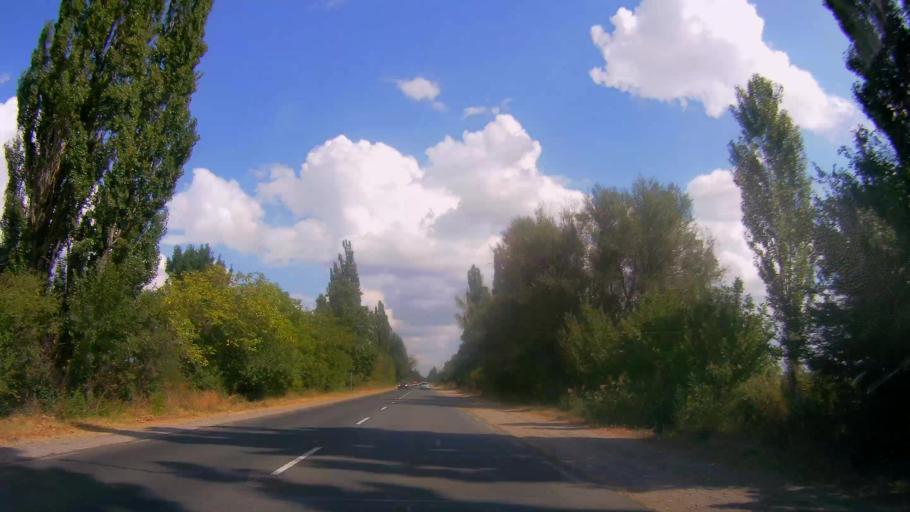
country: BG
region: Sliven
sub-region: Obshtina Sliven
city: Sliven
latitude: 42.6371
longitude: 26.2480
